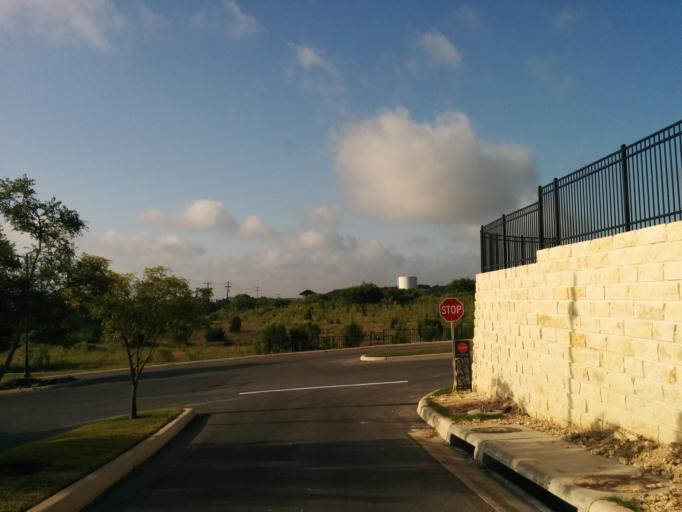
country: US
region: Texas
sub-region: Bexar County
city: Shavano Park
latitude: 29.6090
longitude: -98.6042
